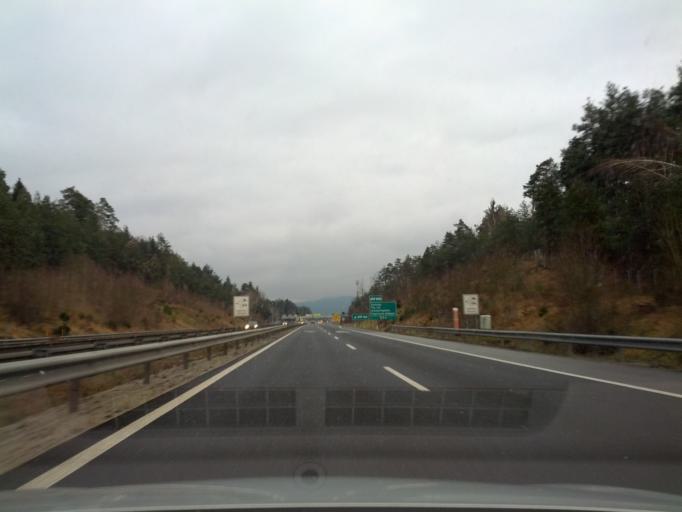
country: SI
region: Vodice
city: Vodice
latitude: 46.1998
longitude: 14.4671
